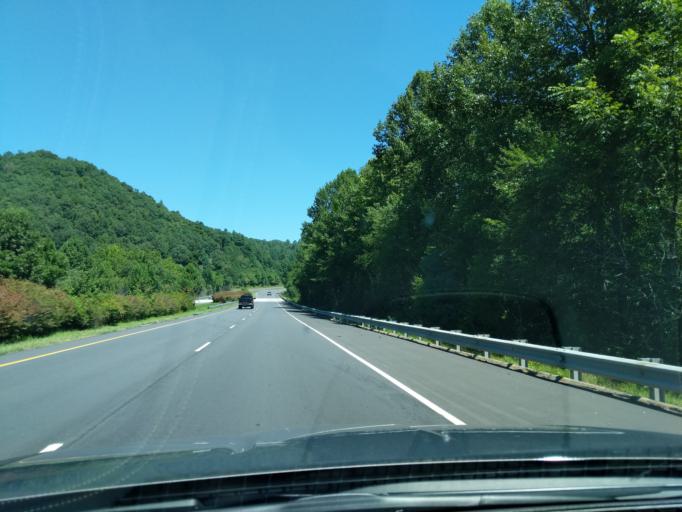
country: US
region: North Carolina
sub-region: Macon County
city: Franklin
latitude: 35.1506
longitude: -83.4665
